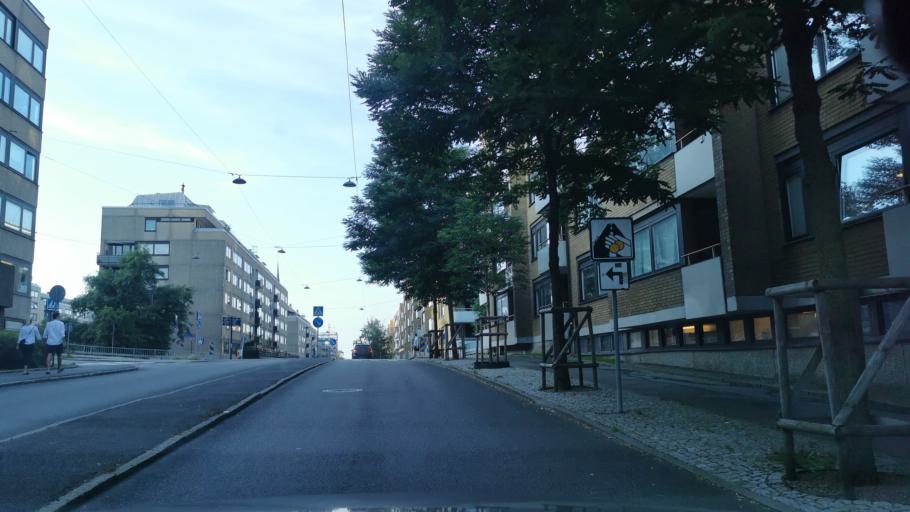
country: SE
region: Vaestra Goetaland
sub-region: Goteborg
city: Goeteborg
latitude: 57.6932
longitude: 11.9481
